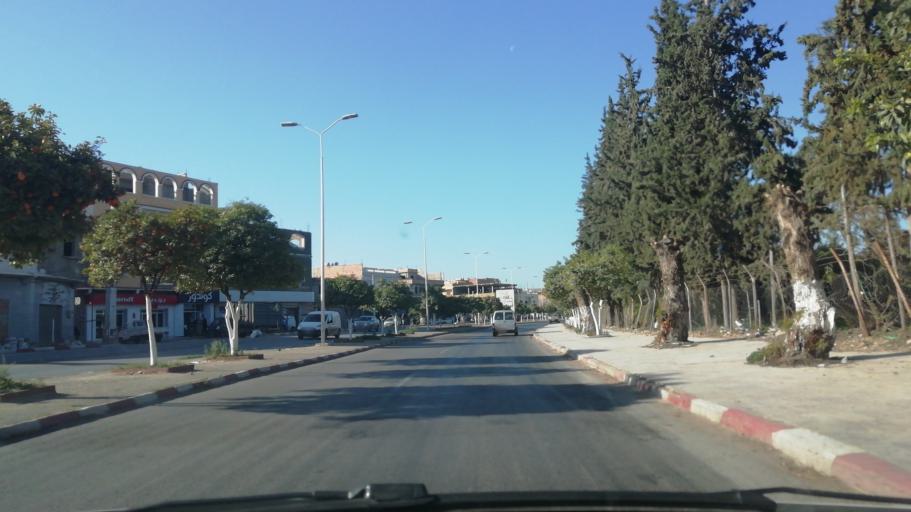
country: DZ
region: Mascara
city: Mascara
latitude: 35.5968
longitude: 0.0786
